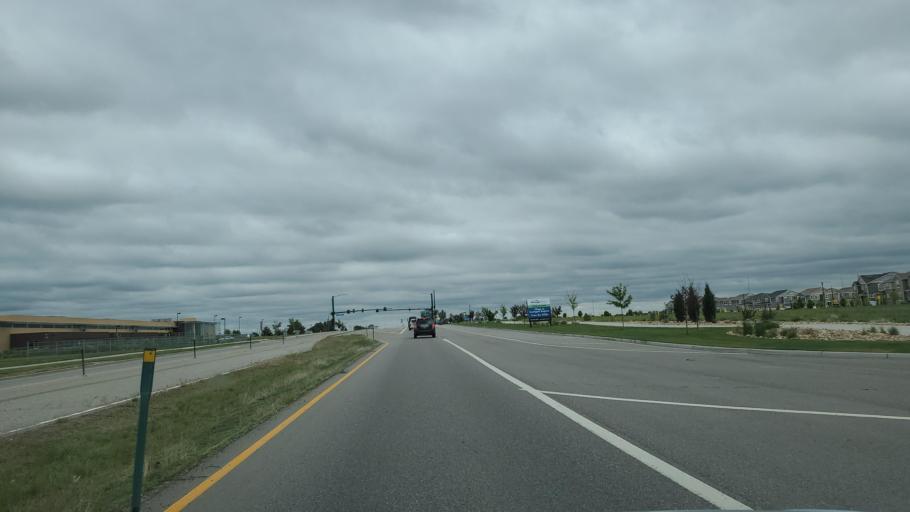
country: US
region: Colorado
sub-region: Adams County
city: Brighton
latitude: 39.9143
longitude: -104.8370
